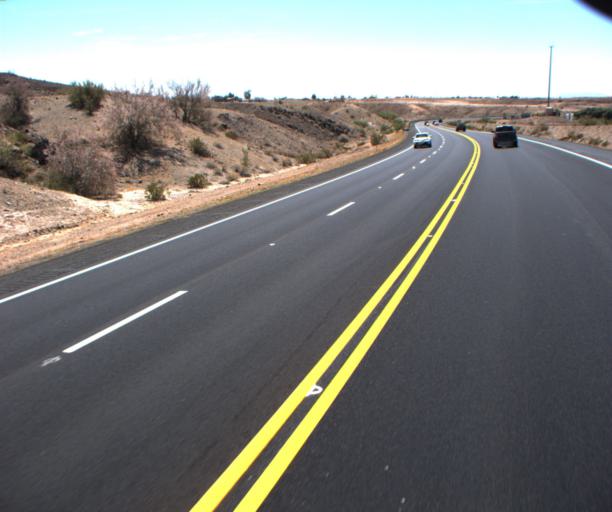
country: US
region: Arizona
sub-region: La Paz County
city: Cienega Springs
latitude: 34.1886
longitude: -114.2138
